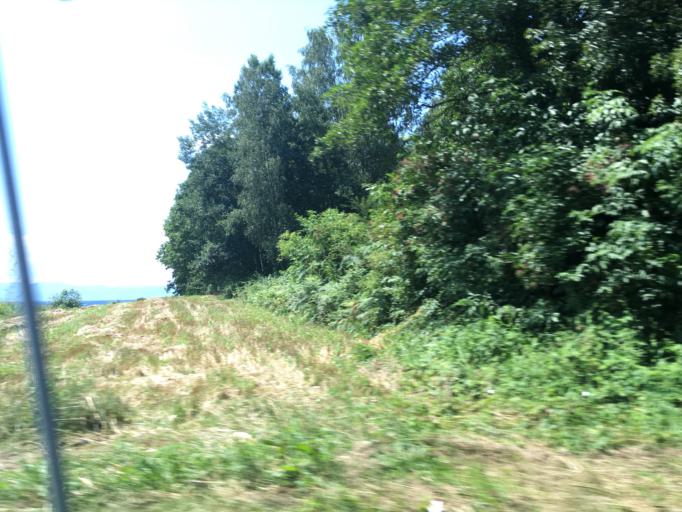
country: SI
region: Metlika
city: Metlika
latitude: 45.5963
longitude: 15.3413
